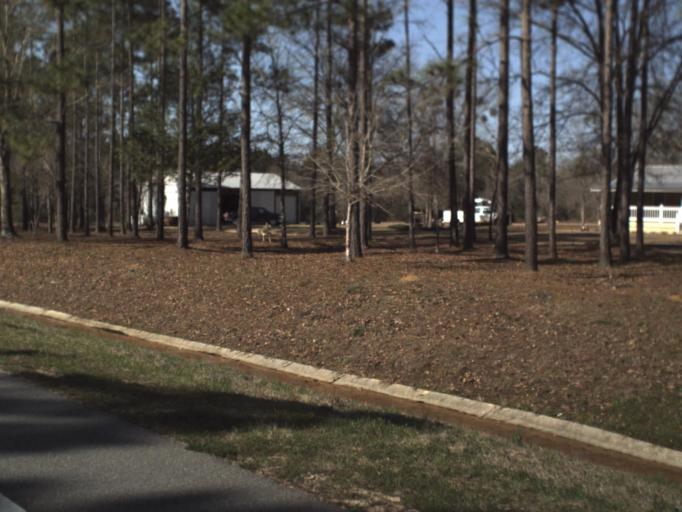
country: US
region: Florida
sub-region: Gulf County
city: Wewahitchka
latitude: 30.2476
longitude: -85.2258
